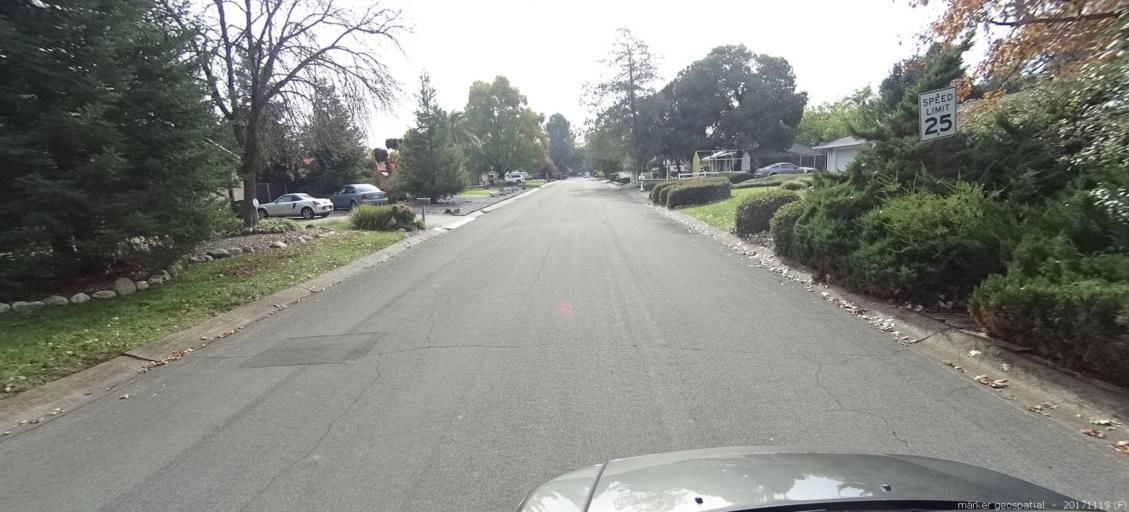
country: US
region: California
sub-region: Shasta County
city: Anderson
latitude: 40.4901
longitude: -122.3105
